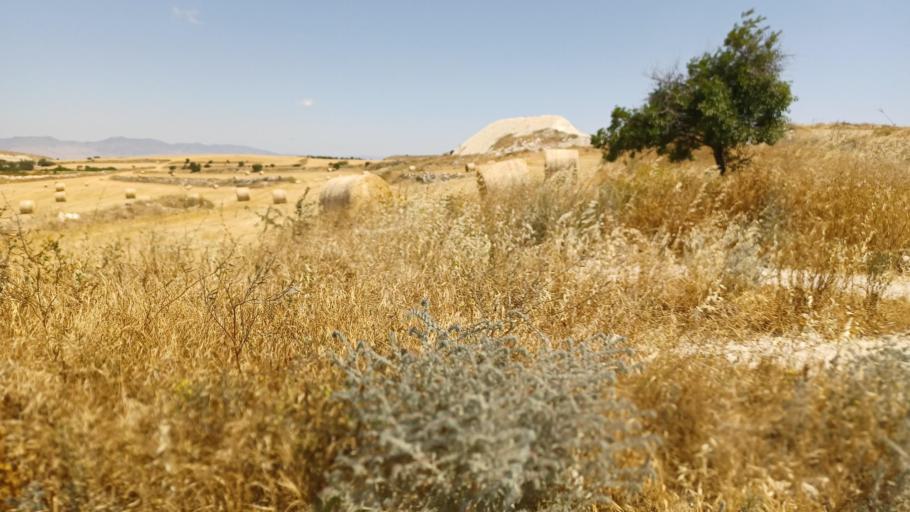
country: CY
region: Larnaka
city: Athienou
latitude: 35.0237
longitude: 33.5275
